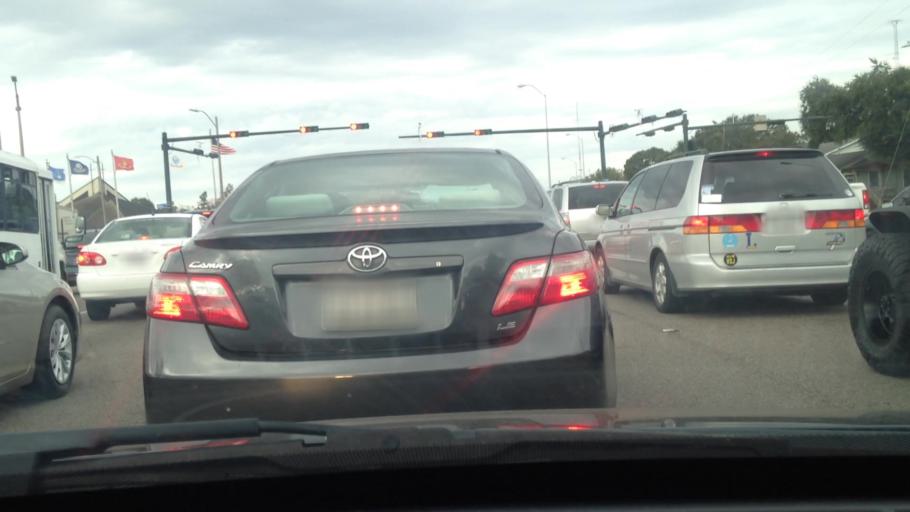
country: US
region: Louisiana
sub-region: Jefferson Parish
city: Terrytown
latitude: 29.9298
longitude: -90.0318
